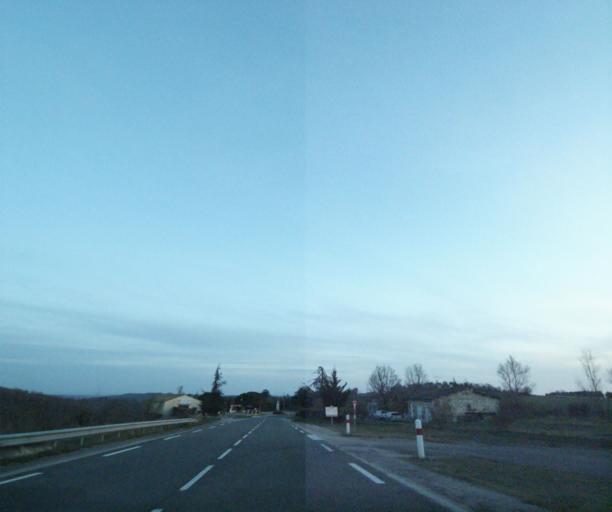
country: FR
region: Midi-Pyrenees
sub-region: Departement du Lot
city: Pradines
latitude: 44.5445
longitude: 1.4767
